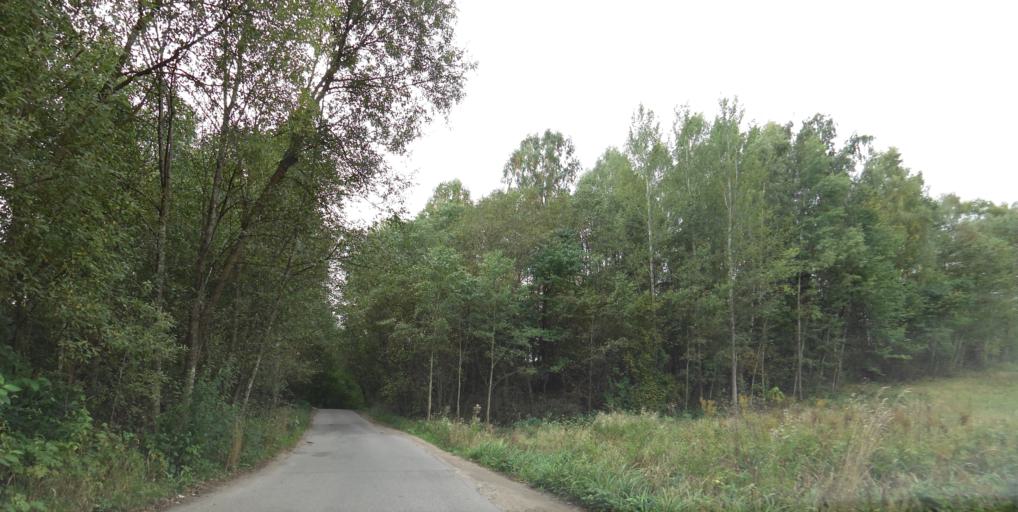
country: LT
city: Grigiskes
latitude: 54.7599
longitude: 25.0380
